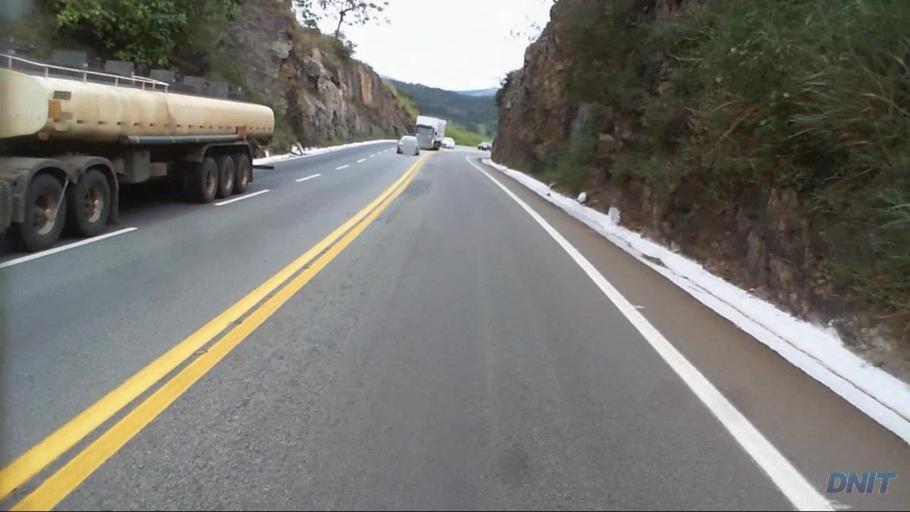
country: BR
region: Minas Gerais
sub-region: Caete
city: Caete
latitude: -19.7865
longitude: -43.7165
